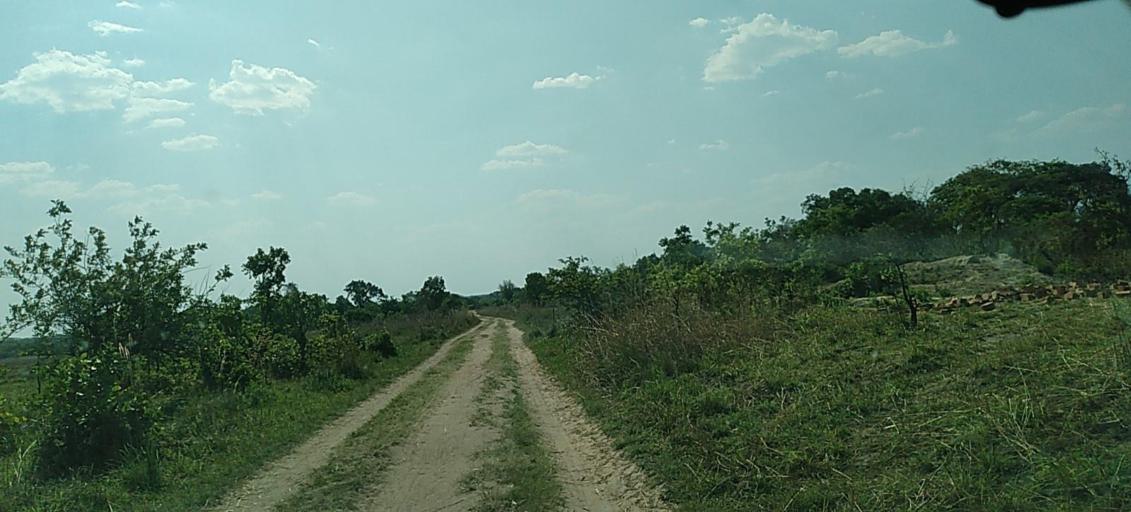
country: ZM
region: North-Western
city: Kalengwa
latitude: -13.1187
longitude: 24.9998
